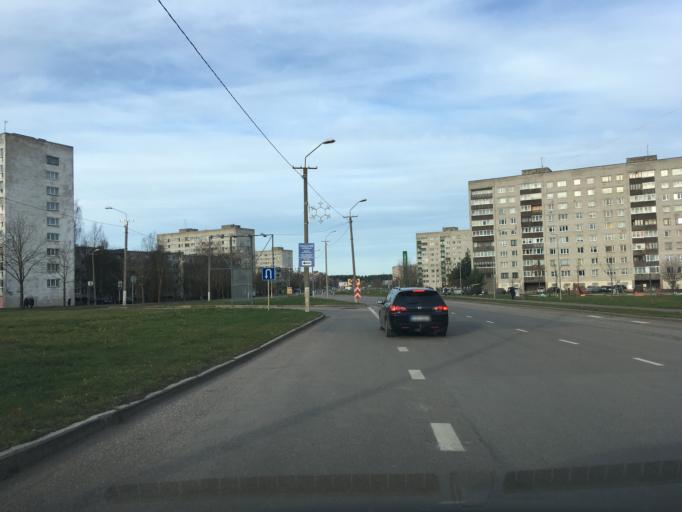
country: EE
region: Ida-Virumaa
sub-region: Narva linn
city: Narva
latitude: 59.3830
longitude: 28.1797
